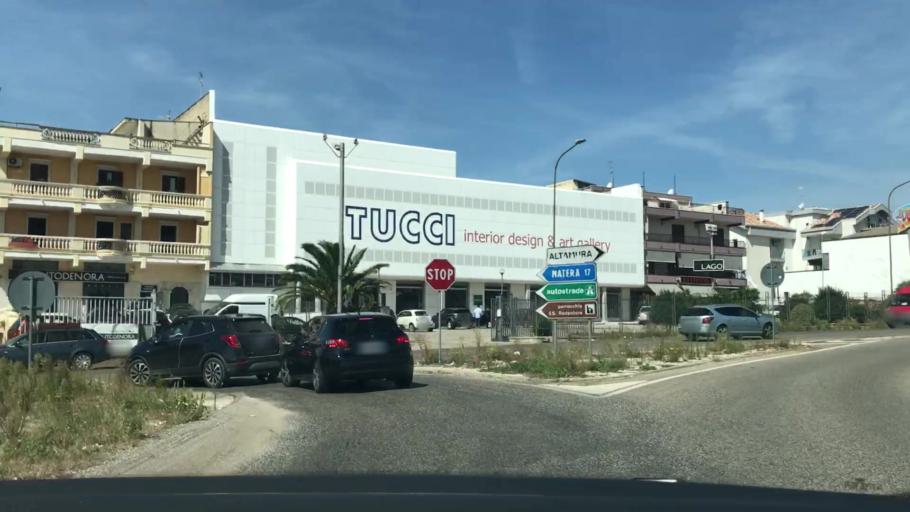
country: IT
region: Apulia
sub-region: Provincia di Bari
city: Altamura
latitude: 40.8161
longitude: 16.5542
